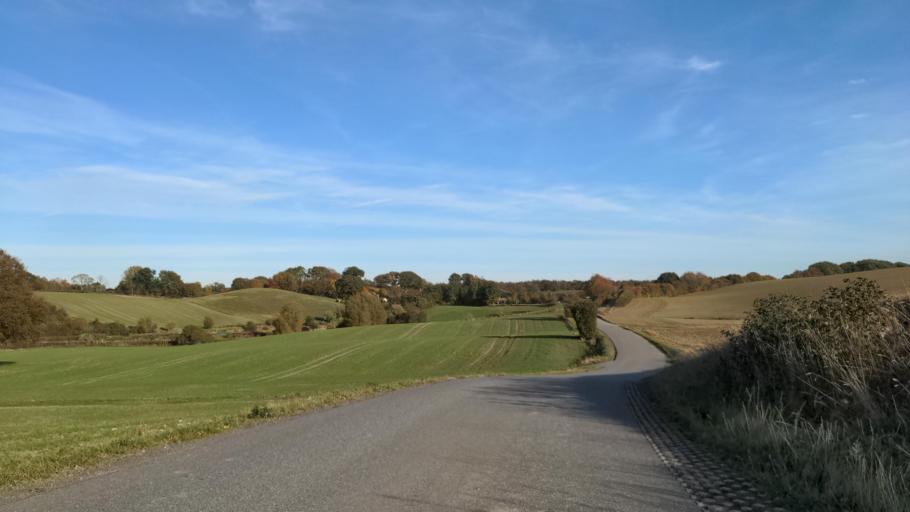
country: DE
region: Schleswig-Holstein
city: Kirchnuchel
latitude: 54.1944
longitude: 10.6897
